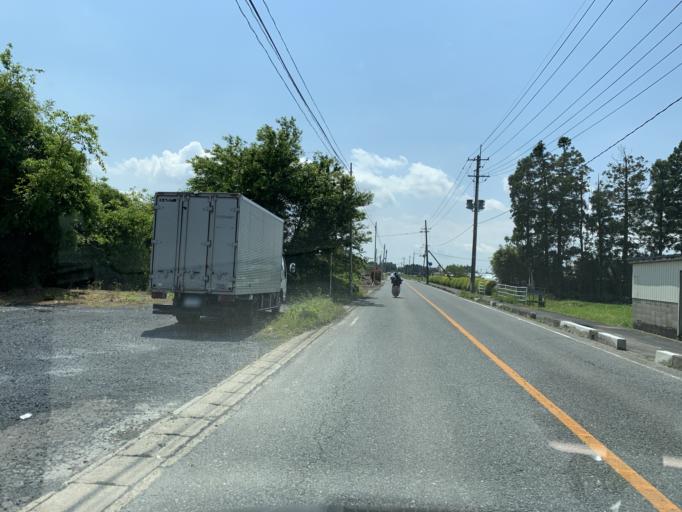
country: JP
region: Miyagi
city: Kogota
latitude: 38.5729
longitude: 141.0377
